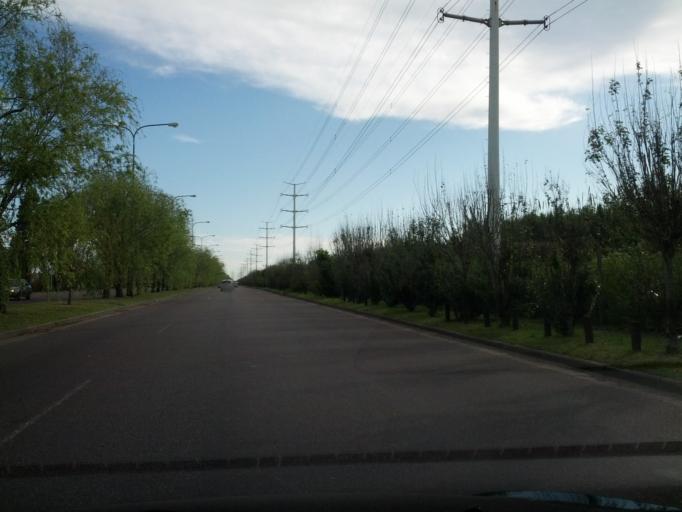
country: AR
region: Buenos Aires F.D.
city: Villa Lugano
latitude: -34.6917
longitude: -58.4502
